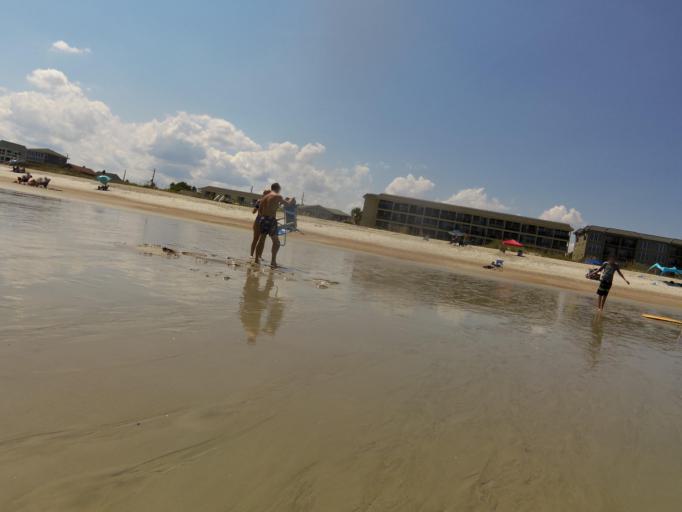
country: US
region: Florida
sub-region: Nassau County
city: Fernandina Beach
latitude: 30.6613
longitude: -81.4307
